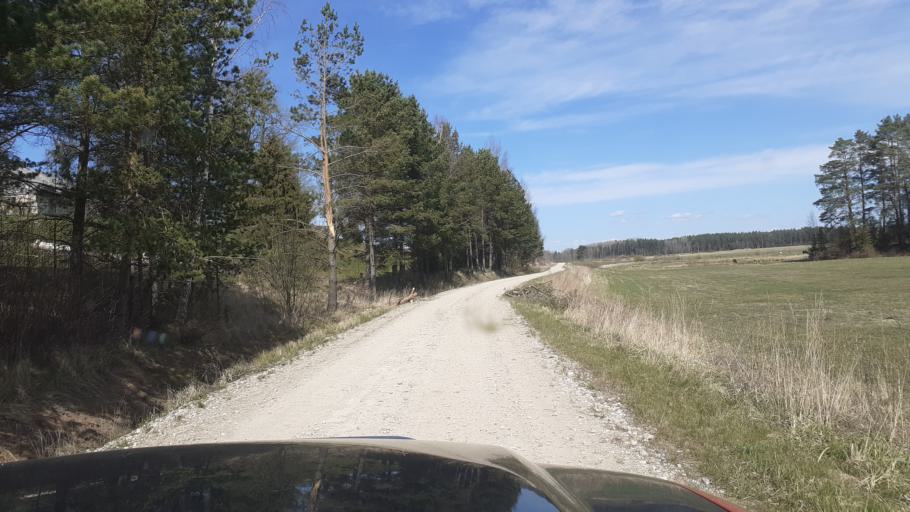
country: LV
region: Kuldigas Rajons
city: Kuldiga
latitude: 56.8382
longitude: 22.0033
